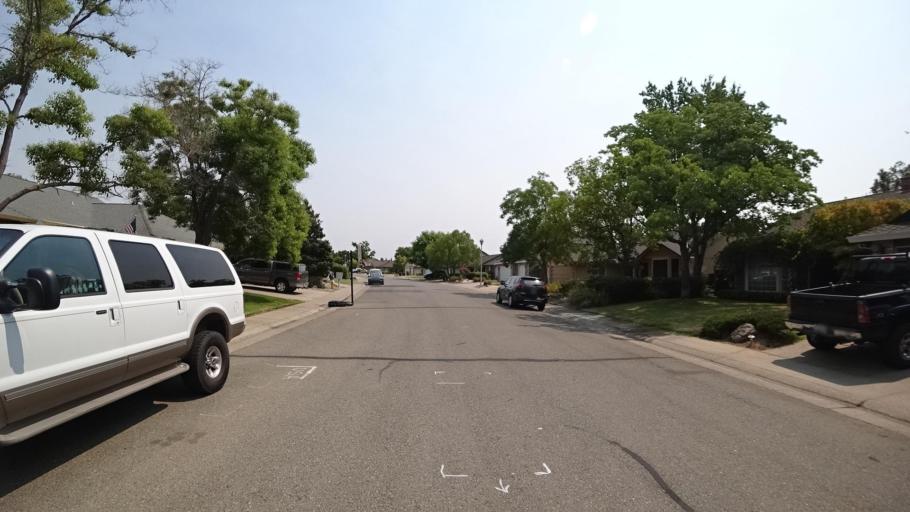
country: US
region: California
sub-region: Placer County
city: Rocklin
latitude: 38.8013
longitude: -121.2568
